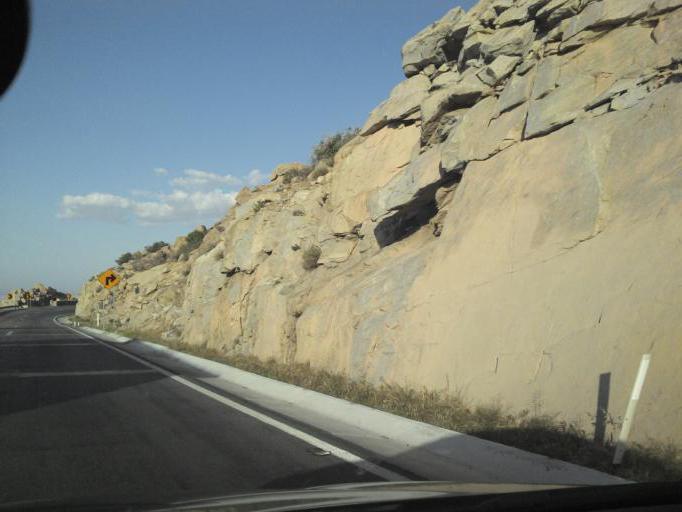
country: MX
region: Baja California
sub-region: Tecate
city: Cereso del Hongo
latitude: 32.5782
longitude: -116.0352
